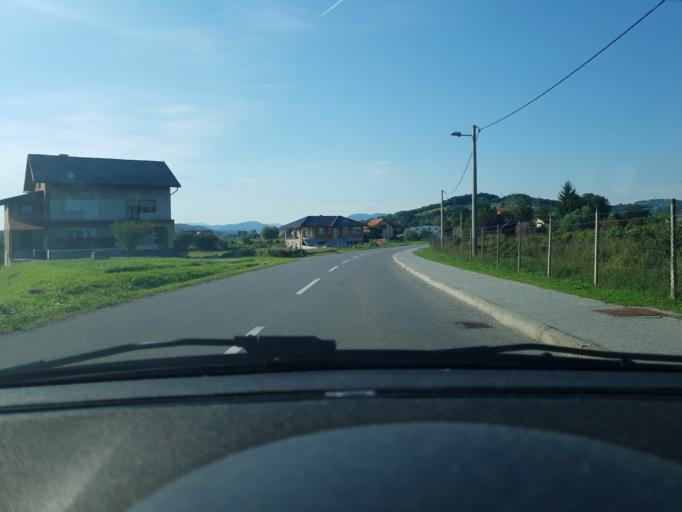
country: HR
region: Krapinsko-Zagorska
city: Zabok
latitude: 46.0669
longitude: 15.9239
